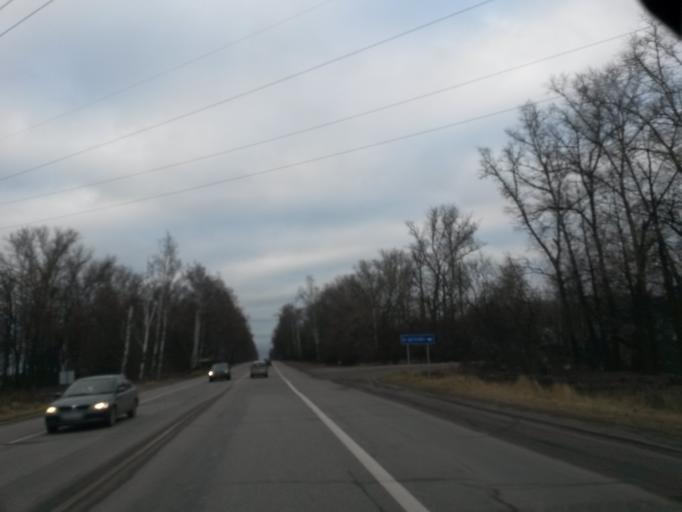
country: RU
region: Moskovskaya
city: Stolbovaya
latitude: 55.2313
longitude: 37.5038
